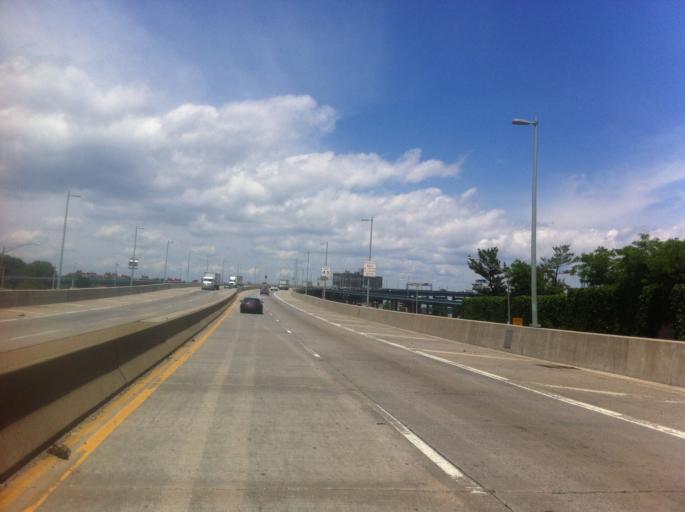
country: US
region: New York
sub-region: Nassau County
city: East Atlantic Beach
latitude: 40.7825
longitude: -73.7853
